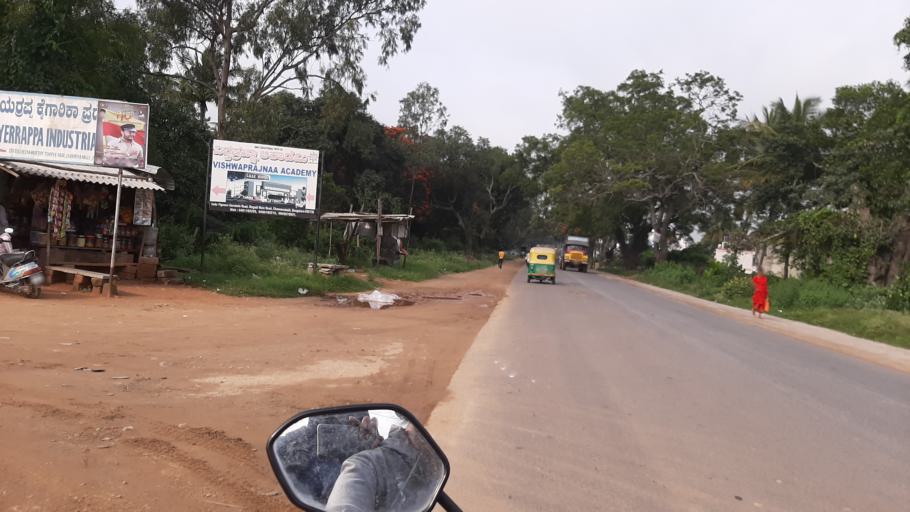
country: IN
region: Karnataka
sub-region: Bangalore Rural
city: Nelamangala
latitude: 12.9798
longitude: 77.4355
